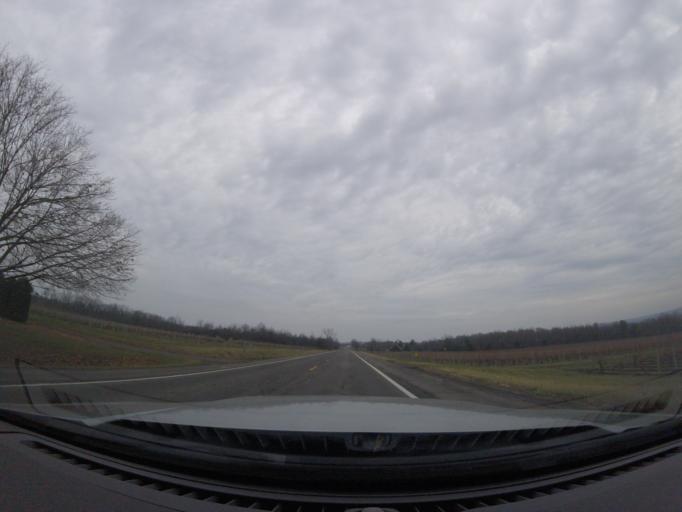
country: US
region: New York
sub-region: Yates County
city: Dundee
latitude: 42.5088
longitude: -76.9237
